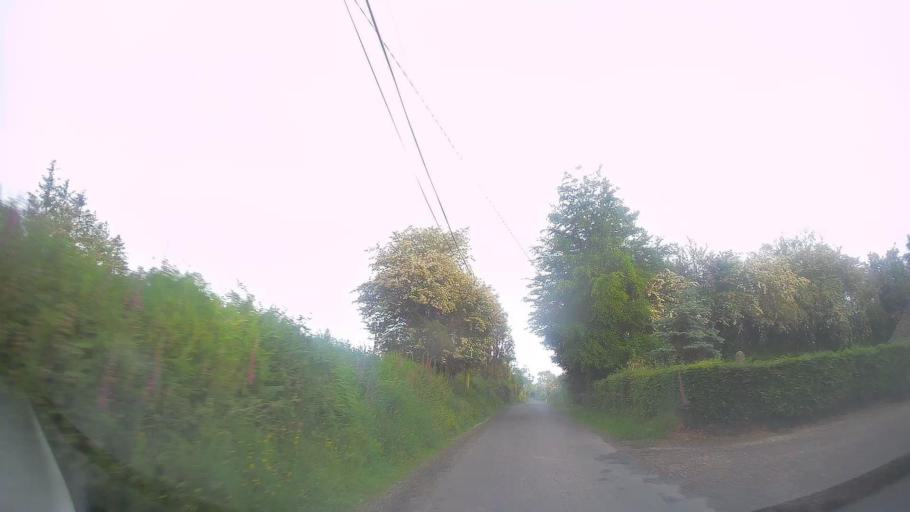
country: IE
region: Munster
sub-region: County Cork
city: Blarney
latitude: 51.9670
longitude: -8.5507
